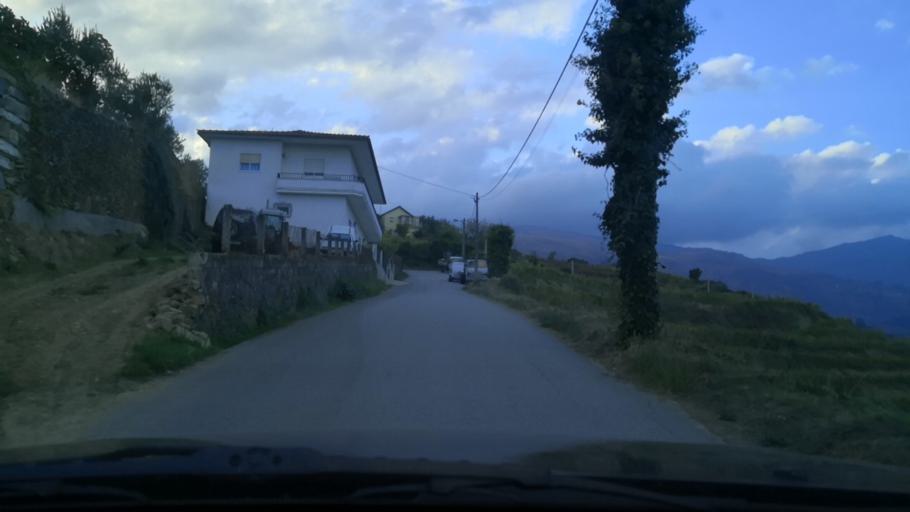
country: PT
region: Vila Real
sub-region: Mesao Frio
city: Mesao Frio
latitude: 41.1824
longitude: -7.8471
